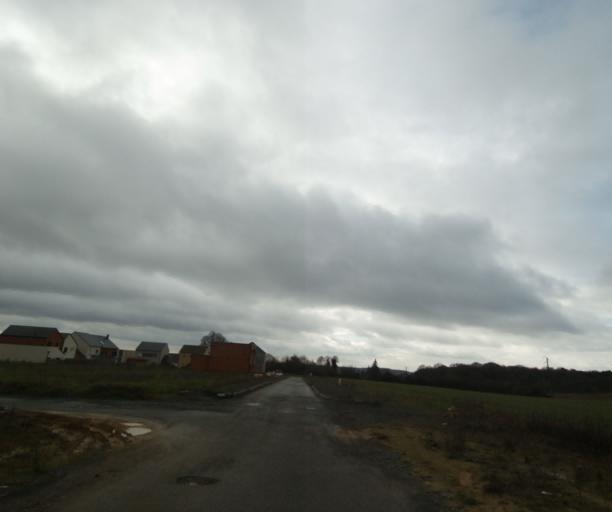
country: FR
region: Pays de la Loire
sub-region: Departement de la Sarthe
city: Rouillon
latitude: 48.0202
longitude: 0.1443
